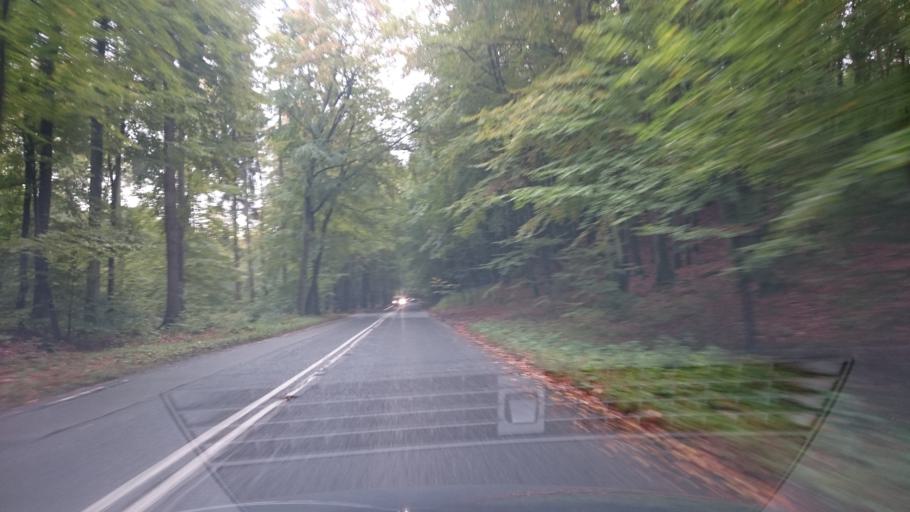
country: PL
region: Pomeranian Voivodeship
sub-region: Gdynia
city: Wielki Kack
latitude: 54.4581
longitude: 18.5122
